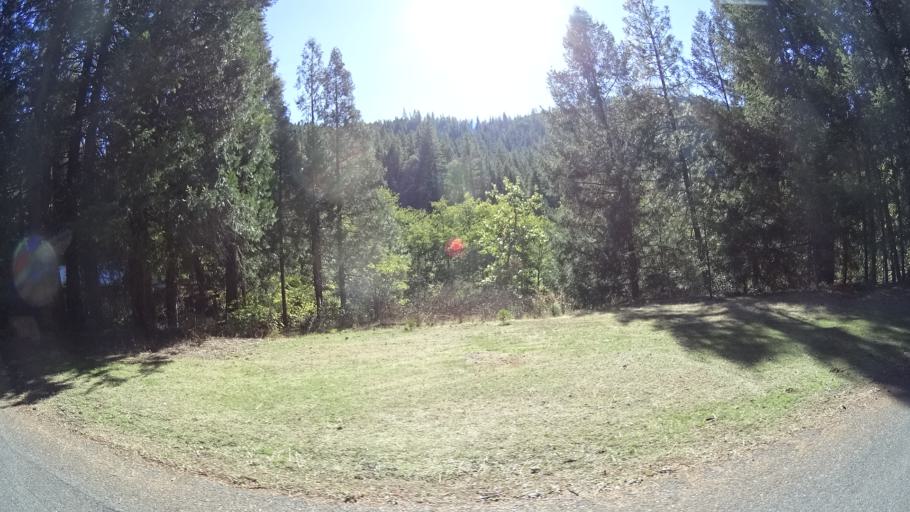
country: US
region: California
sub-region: Siskiyou County
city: Happy Camp
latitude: 41.3009
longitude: -123.1384
